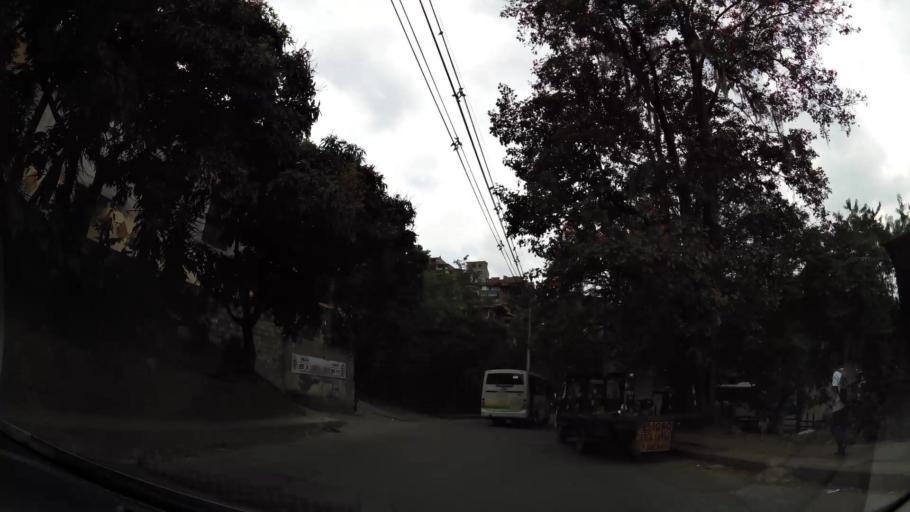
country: CO
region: Antioquia
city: Medellin
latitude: 6.2470
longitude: -75.5462
